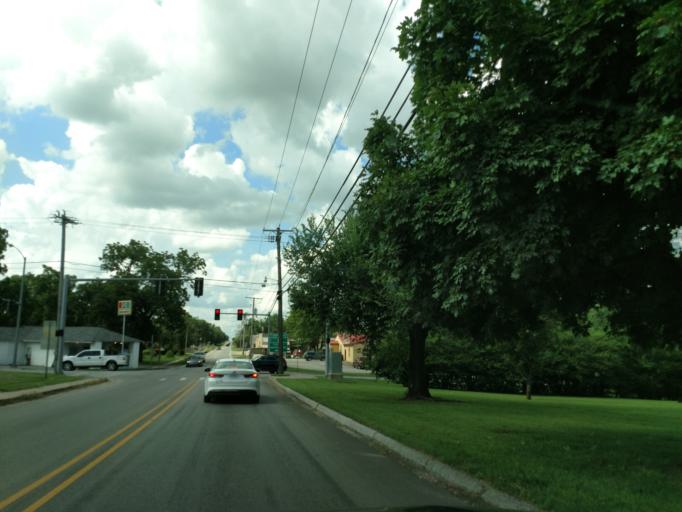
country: US
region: Arkansas
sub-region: Carroll County
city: Berryville
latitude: 36.3700
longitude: -93.5672
